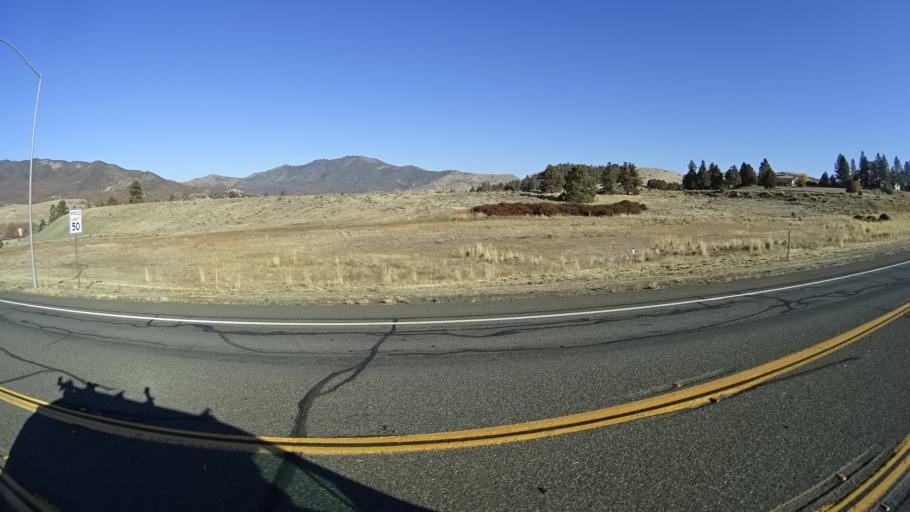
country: US
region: California
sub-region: Siskiyou County
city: Yreka
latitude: 41.7382
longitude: -122.6226
